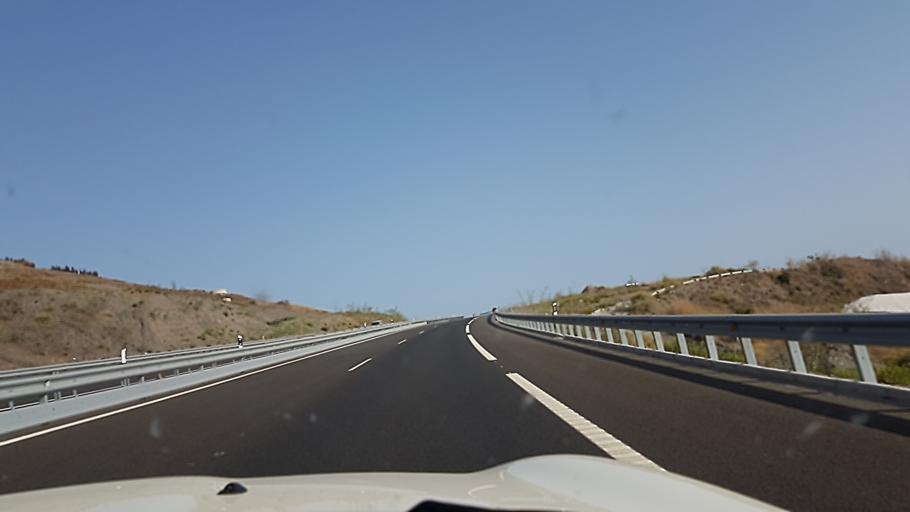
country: ES
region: Andalusia
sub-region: Provincia de Granada
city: Albunol
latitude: 36.7540
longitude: -3.2189
